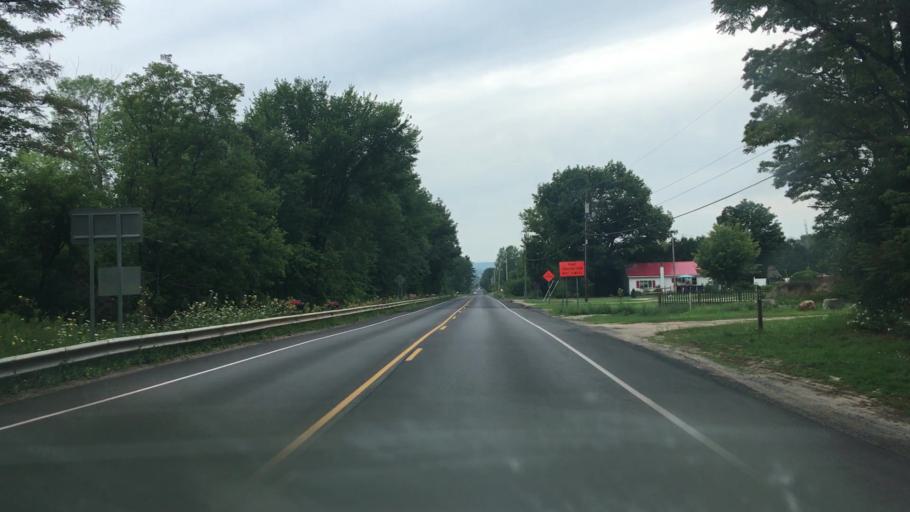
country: US
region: New York
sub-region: Clinton County
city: Plattsburgh West
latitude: 44.6527
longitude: -73.5127
